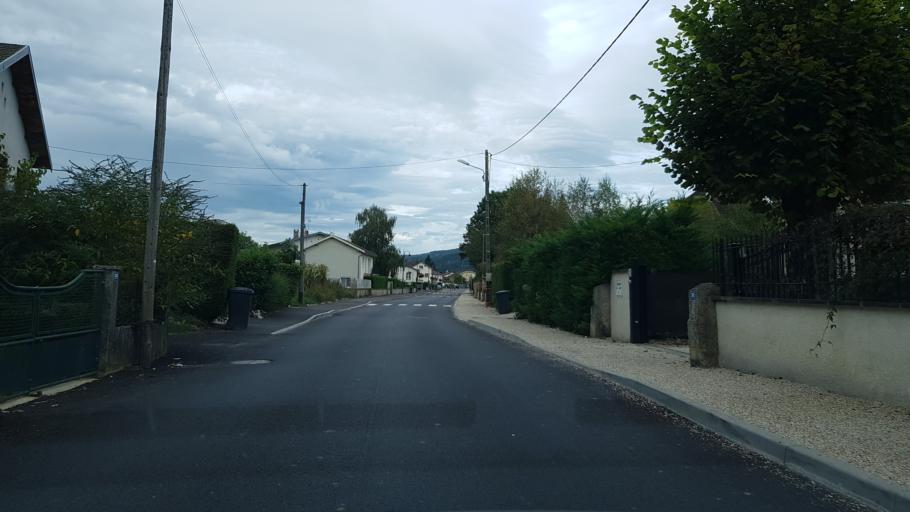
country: FR
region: Rhone-Alpes
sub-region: Departement de l'Ain
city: Villereversure
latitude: 46.1902
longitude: 5.3942
